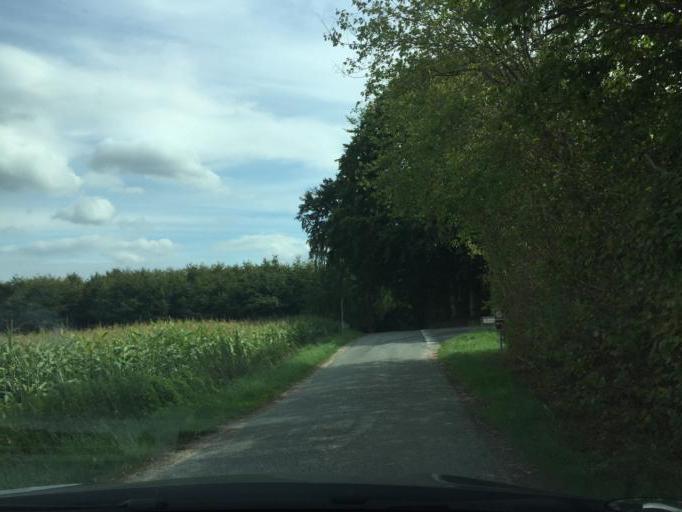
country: DK
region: South Denmark
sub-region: Nordfyns Kommune
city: Sonderso
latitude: 55.4093
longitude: 10.2269
